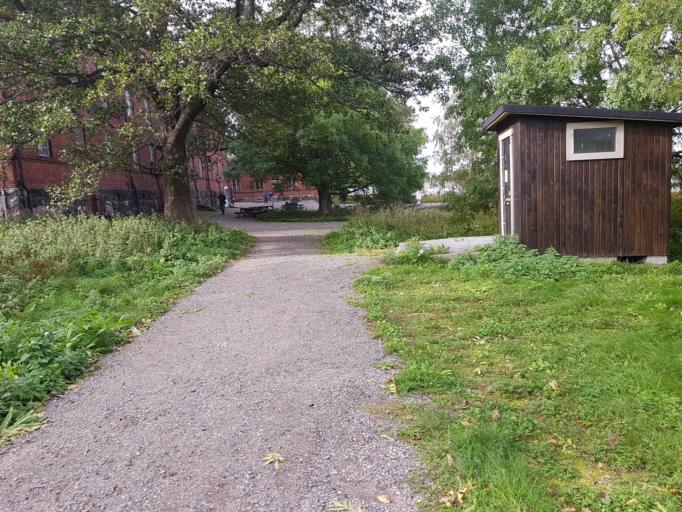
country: FI
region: Uusimaa
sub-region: Helsinki
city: Helsinki
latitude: 60.1400
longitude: 25.0079
